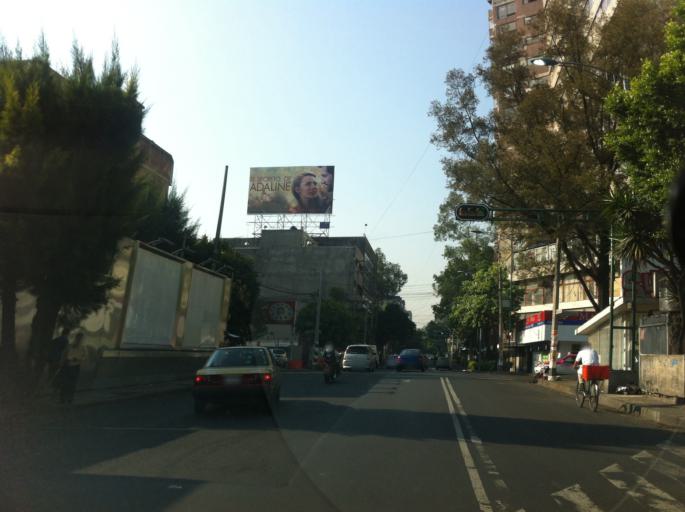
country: MX
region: Mexico City
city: Benito Juarez
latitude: 19.4151
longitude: -99.1654
